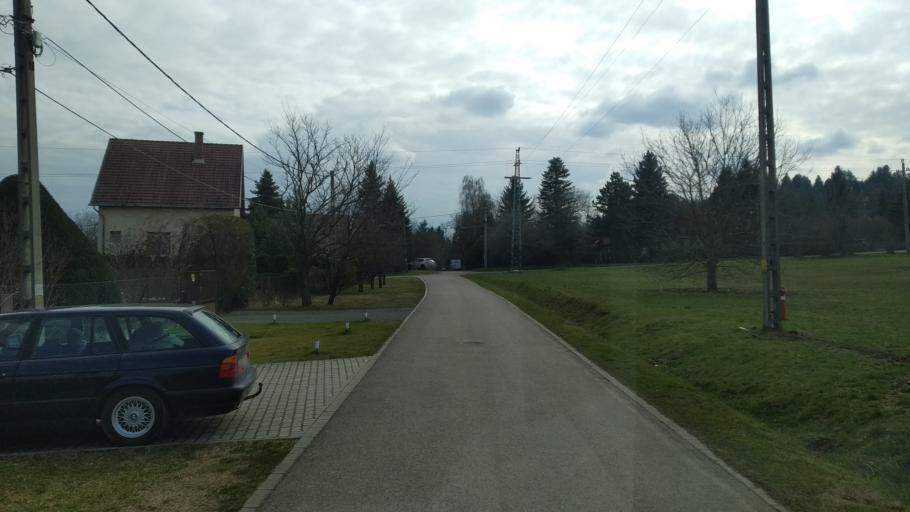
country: HU
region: Pest
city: Tahitotfalu
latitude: 47.7601
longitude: 19.0672
